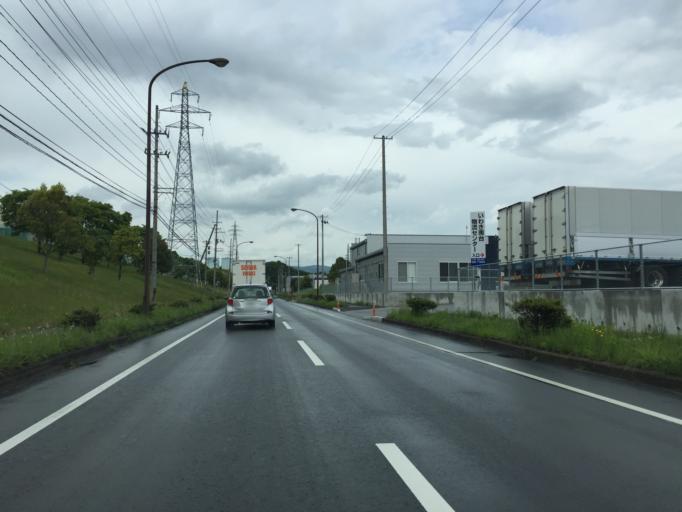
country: JP
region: Ibaraki
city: Kitaibaraki
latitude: 36.9366
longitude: 140.7469
